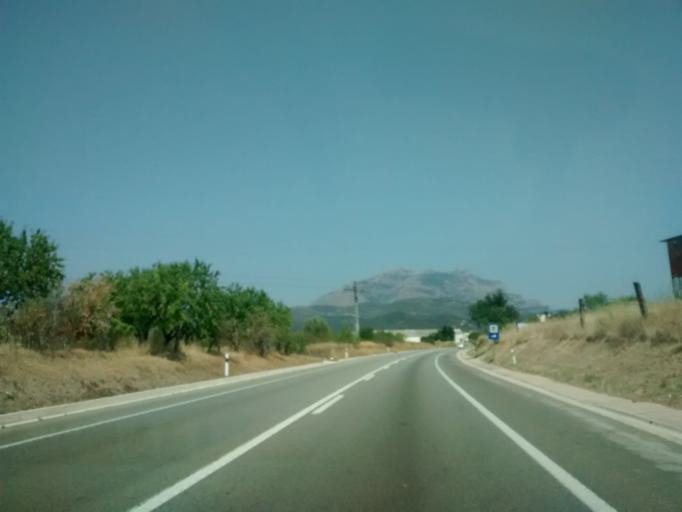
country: ES
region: Catalonia
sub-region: Provincia de Barcelona
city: Olesa de Montserrat
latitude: 41.5384
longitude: 1.8899
